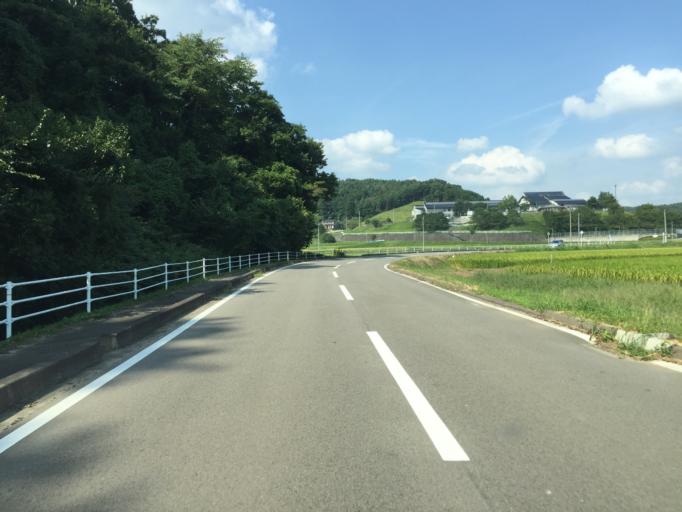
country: JP
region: Fukushima
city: Nihommatsu
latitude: 37.5819
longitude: 140.3839
